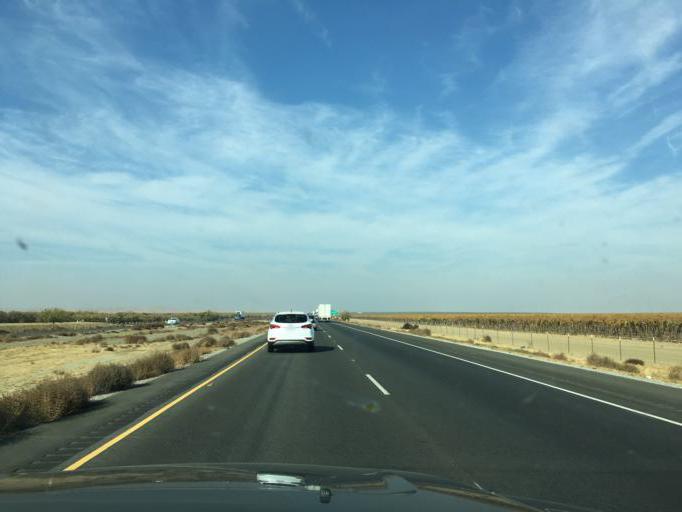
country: US
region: California
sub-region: Kings County
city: Kettleman City
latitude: 35.9180
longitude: -119.8949
